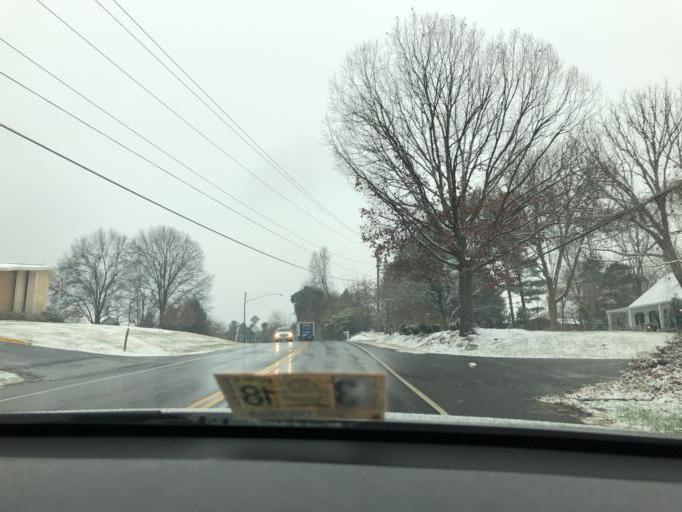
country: US
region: Virginia
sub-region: Fairfax County
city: Oakton
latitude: 38.8928
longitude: -77.3042
